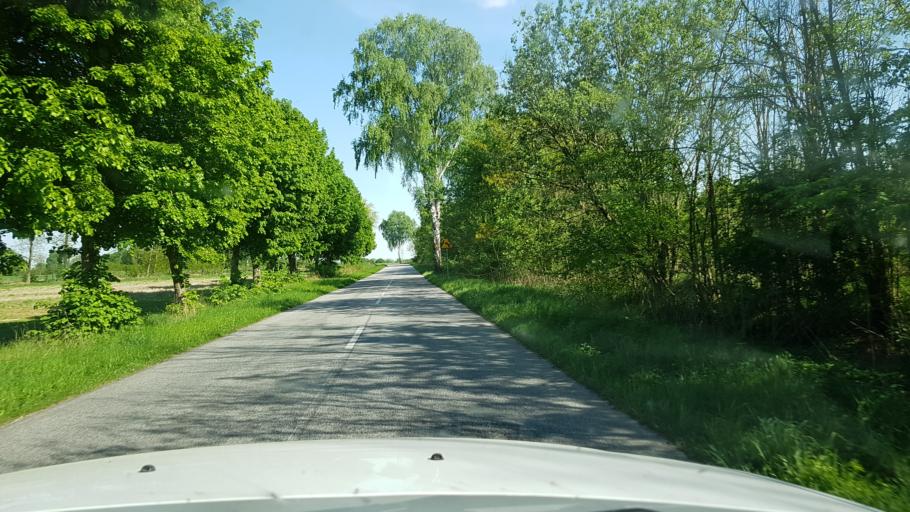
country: PL
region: West Pomeranian Voivodeship
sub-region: Powiat lobeski
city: Resko
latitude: 53.8125
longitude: 15.4069
